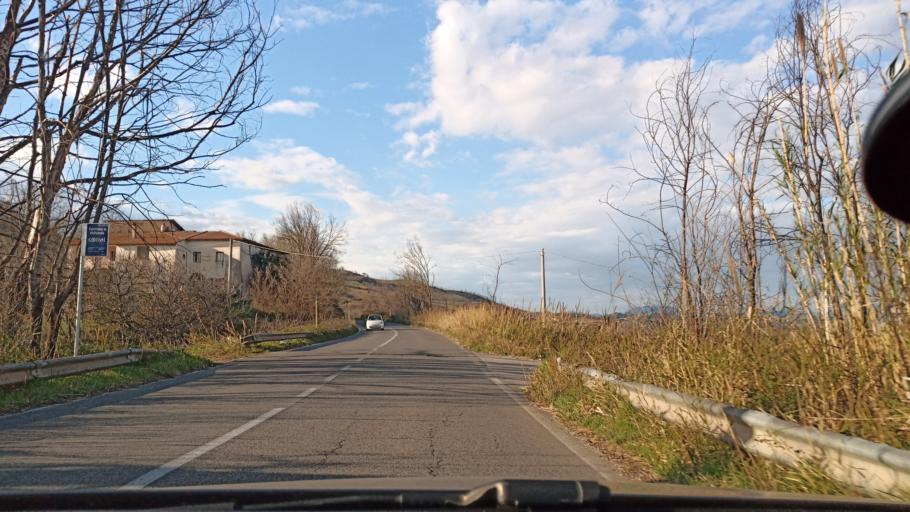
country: IT
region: Latium
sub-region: Citta metropolitana di Roma Capitale
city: Fiano Romano
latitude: 42.1861
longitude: 12.6047
